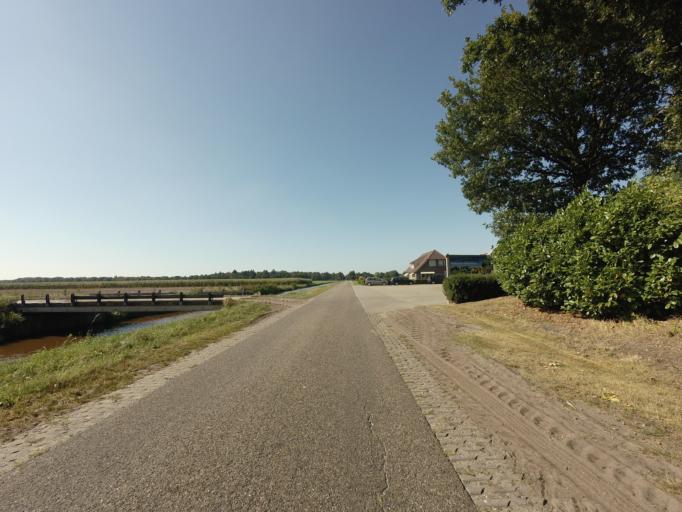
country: NL
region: Overijssel
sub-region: Gemeente Hardenberg
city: Hardenberg
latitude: 52.5282
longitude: 6.6475
